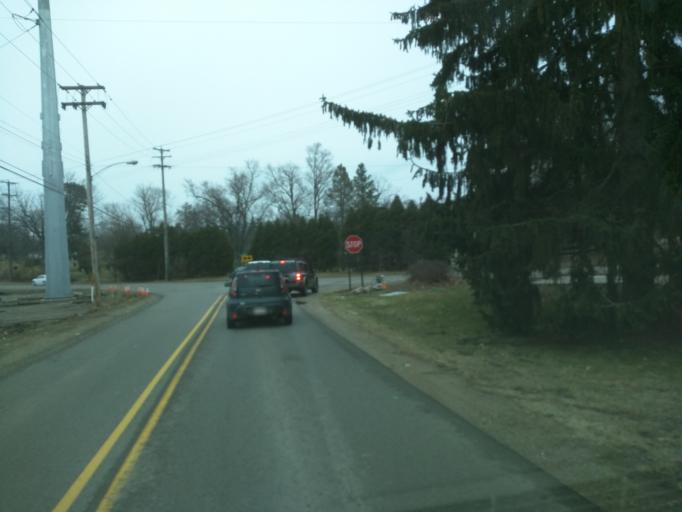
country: US
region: Michigan
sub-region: Eaton County
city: Waverly
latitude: 42.7120
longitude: -84.6060
